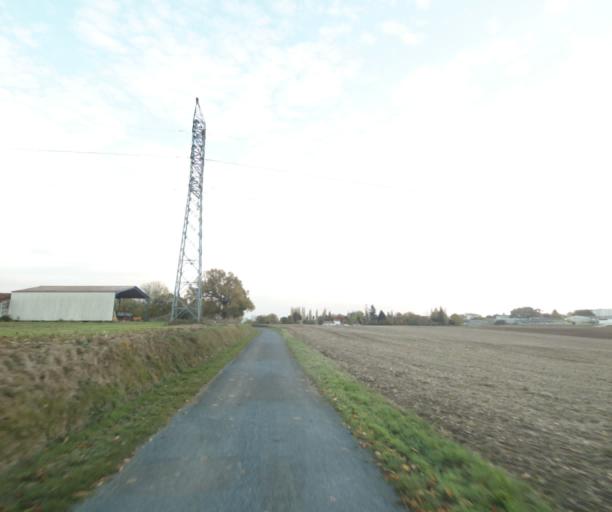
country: FR
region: Poitou-Charentes
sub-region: Departement de la Charente-Maritime
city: Saintes
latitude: 45.7650
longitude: -0.6490
